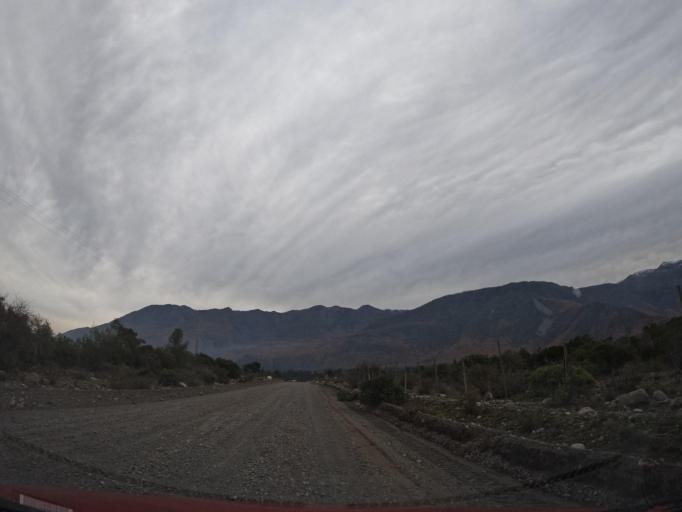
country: CL
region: Maule
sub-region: Provincia de Linares
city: Colbun
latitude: -35.7078
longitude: -71.0753
